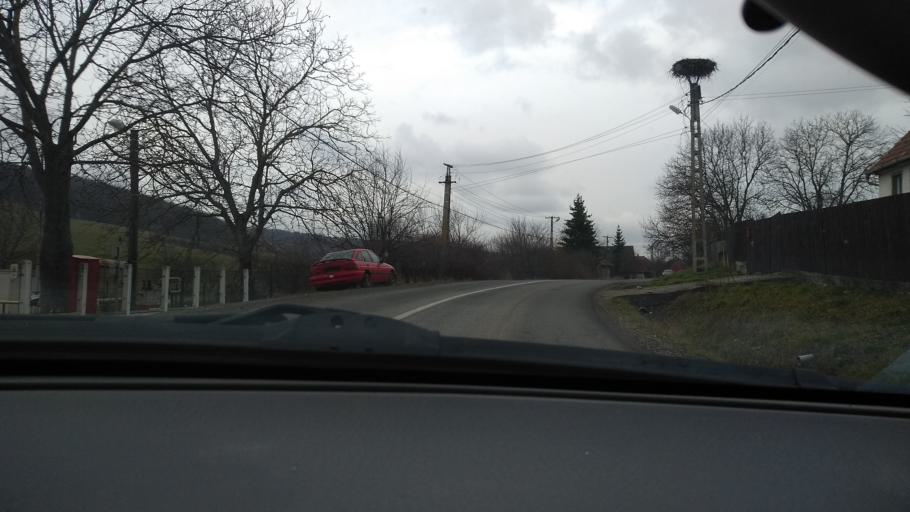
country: RO
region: Mures
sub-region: Comuna Galesti
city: Galesti
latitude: 46.5288
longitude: 24.7708
